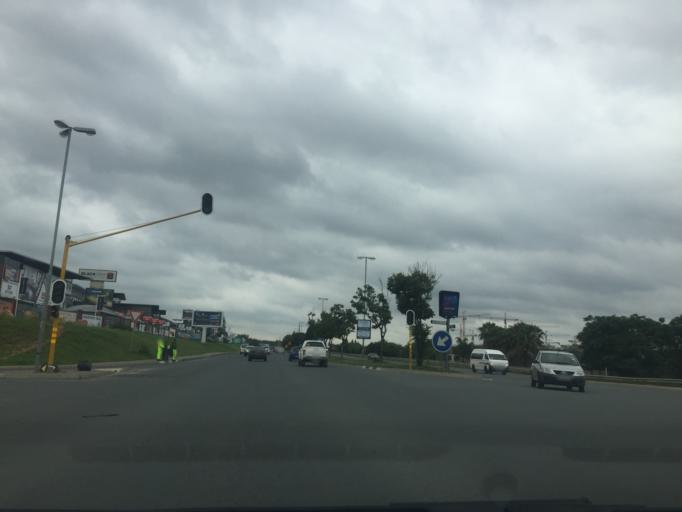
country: ZA
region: Gauteng
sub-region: City of Johannesburg Metropolitan Municipality
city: Diepsloot
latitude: -26.0121
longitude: 28.0113
